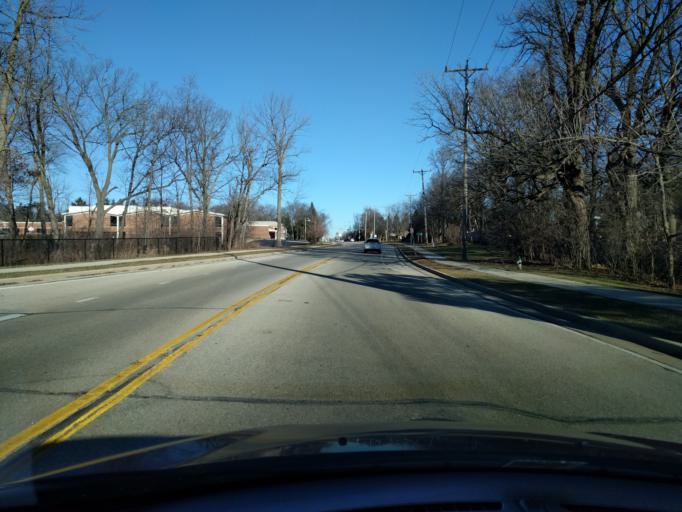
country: US
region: Wisconsin
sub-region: Milwaukee County
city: River Hills
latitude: 43.1674
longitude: -87.9121
